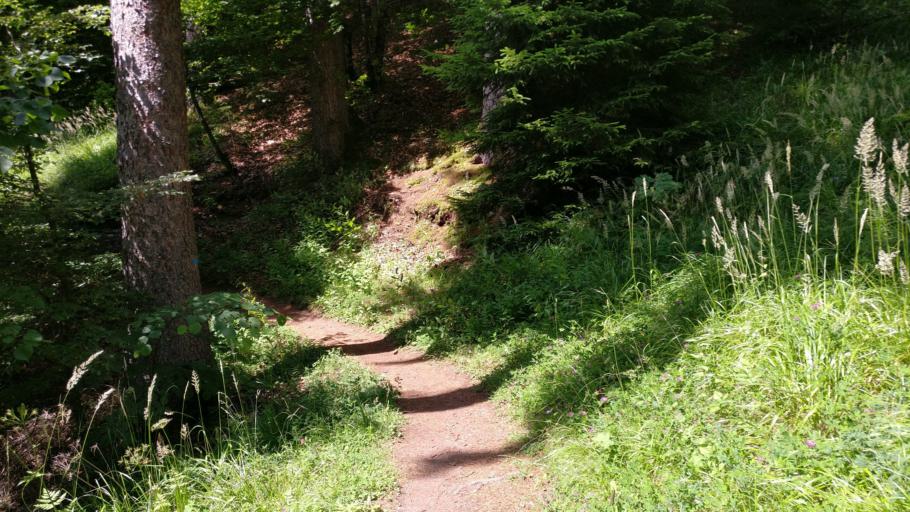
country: IT
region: Trentino-Alto Adige
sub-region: Provincia di Trento
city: Ruffre
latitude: 46.4209
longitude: 11.1998
